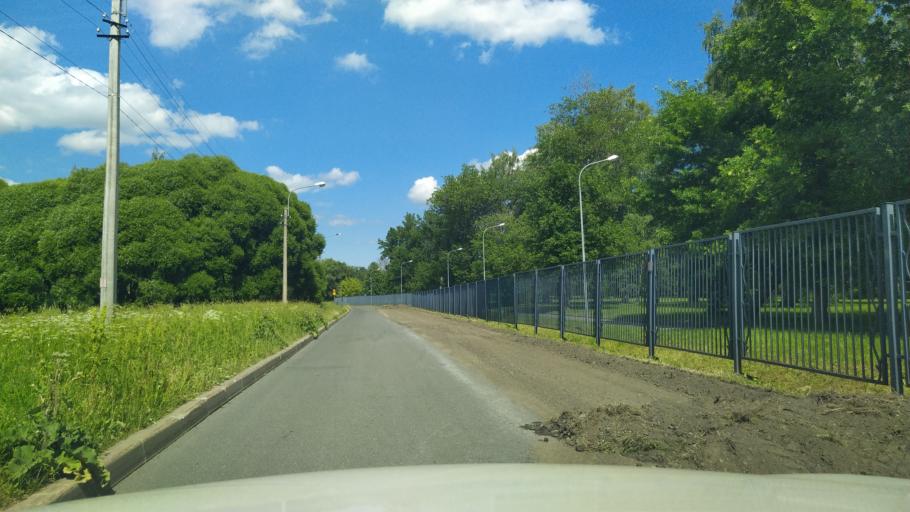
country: RU
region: Leningrad
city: Akademicheskoe
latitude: 59.9983
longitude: 30.4175
